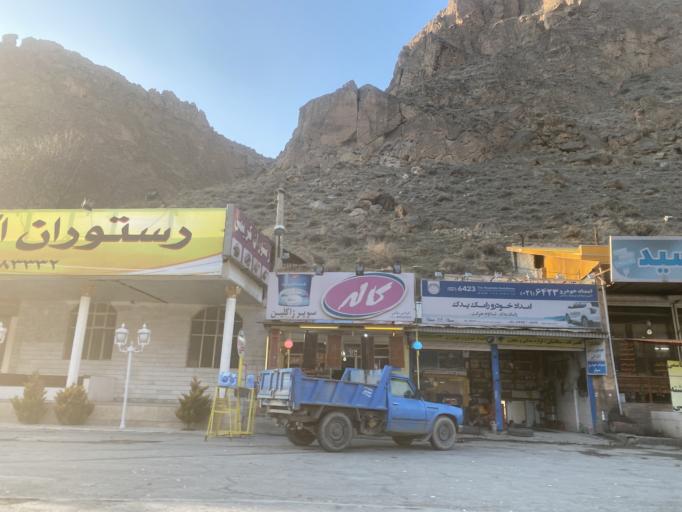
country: IR
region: Tehran
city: Damavand
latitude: 35.8794
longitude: 52.1840
